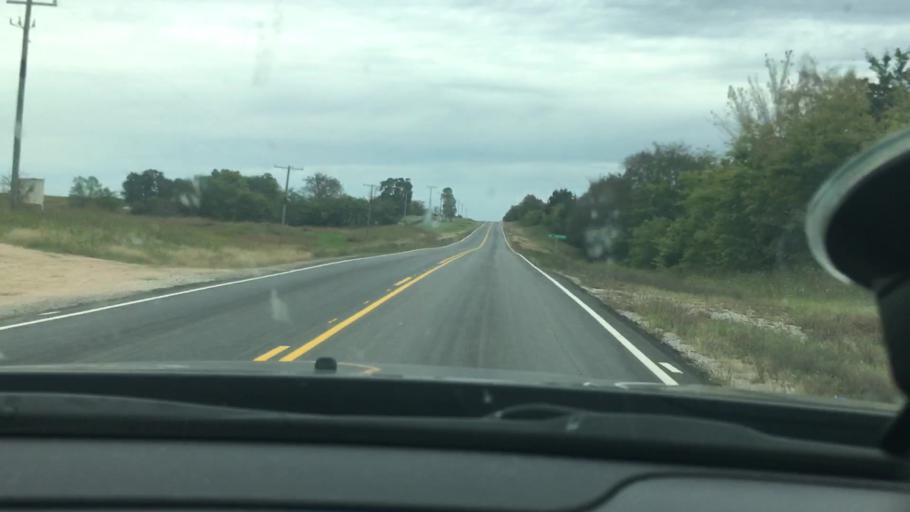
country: US
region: Oklahoma
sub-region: Coal County
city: Coalgate
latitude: 34.3856
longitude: -96.4245
